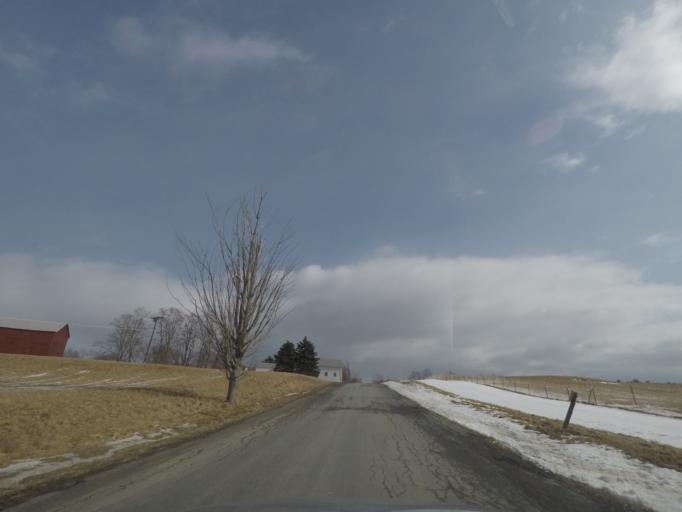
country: US
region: New York
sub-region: Rensselaer County
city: Poestenkill
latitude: 42.7811
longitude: -73.5586
